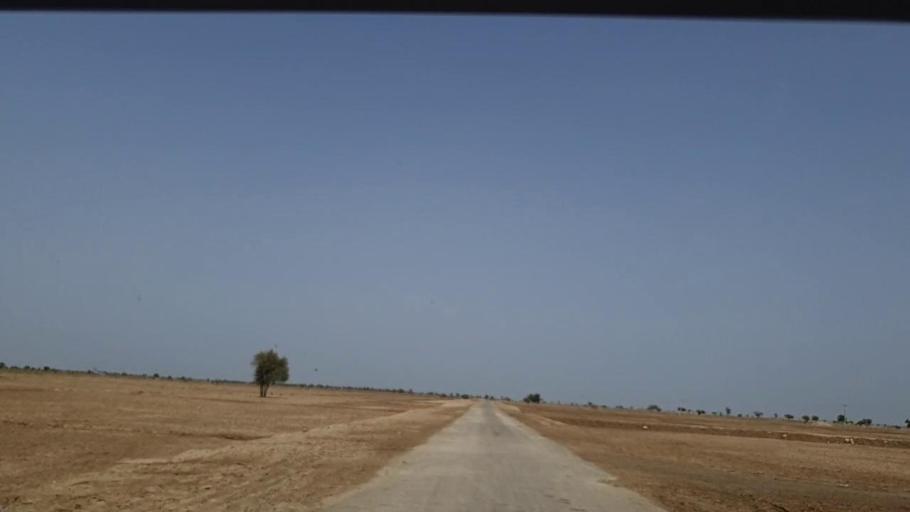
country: PK
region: Sindh
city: Johi
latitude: 26.7707
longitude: 67.6477
